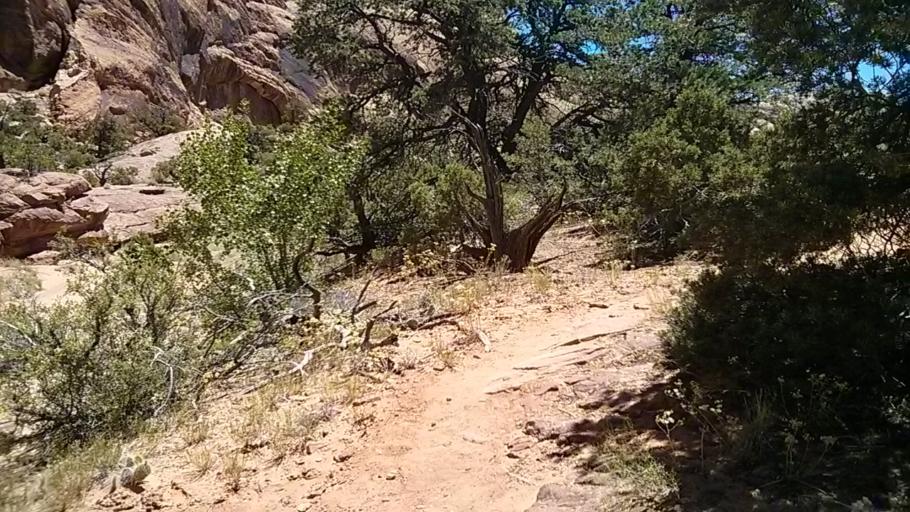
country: US
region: Utah
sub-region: Grand County
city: Moab
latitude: 38.4436
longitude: -109.9158
